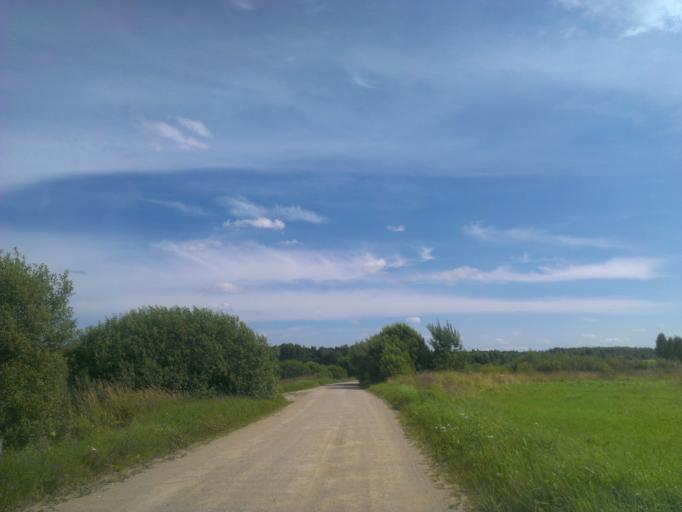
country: LV
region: Ligatne
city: Ligatne
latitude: 57.2221
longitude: 25.0056
